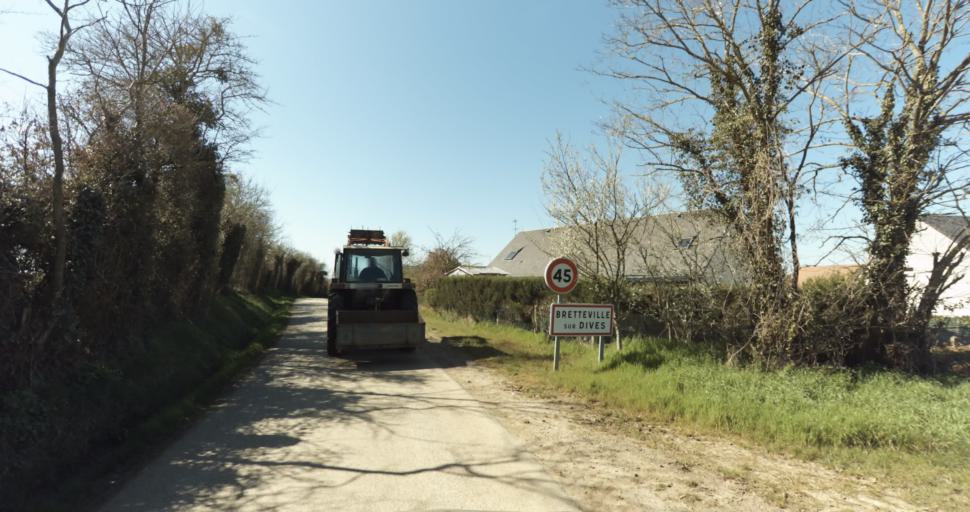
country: FR
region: Lower Normandy
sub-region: Departement du Calvados
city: Saint-Pierre-sur-Dives
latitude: 49.0377
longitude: -0.0153
